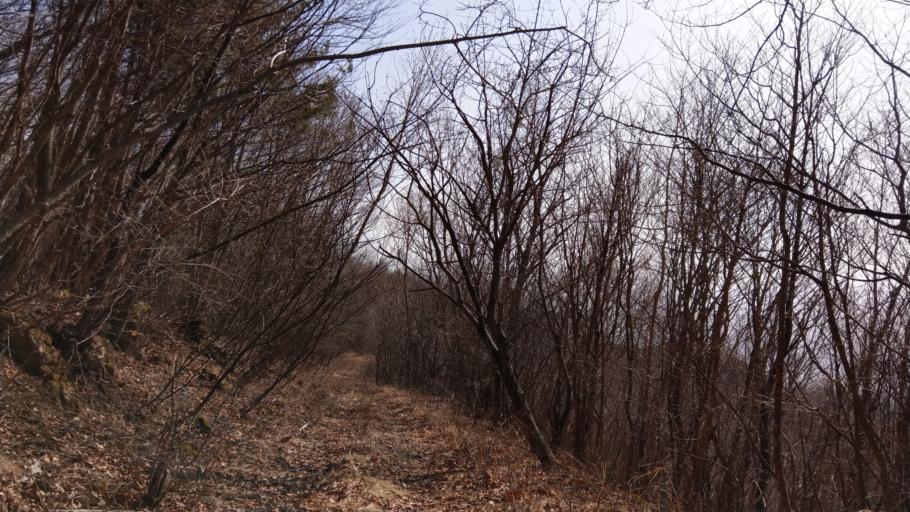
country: JP
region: Nagano
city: Komoro
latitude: 36.3816
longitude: 138.4398
